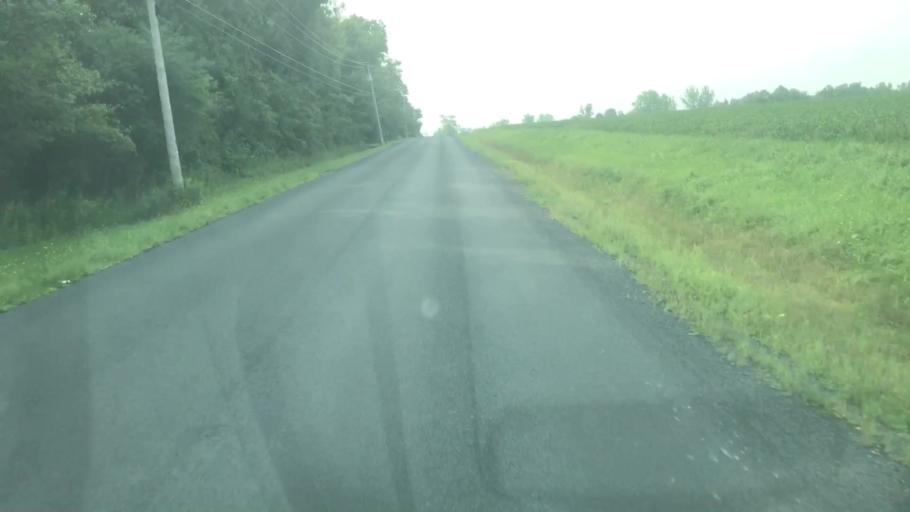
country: US
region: New York
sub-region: Onondaga County
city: Skaneateles
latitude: 42.9355
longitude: -76.4579
